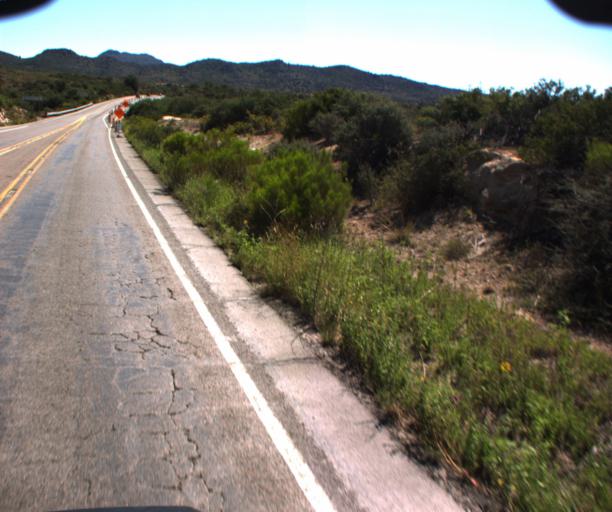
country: US
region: Arizona
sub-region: Pinal County
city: Superior
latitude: 33.3135
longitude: -111.0476
